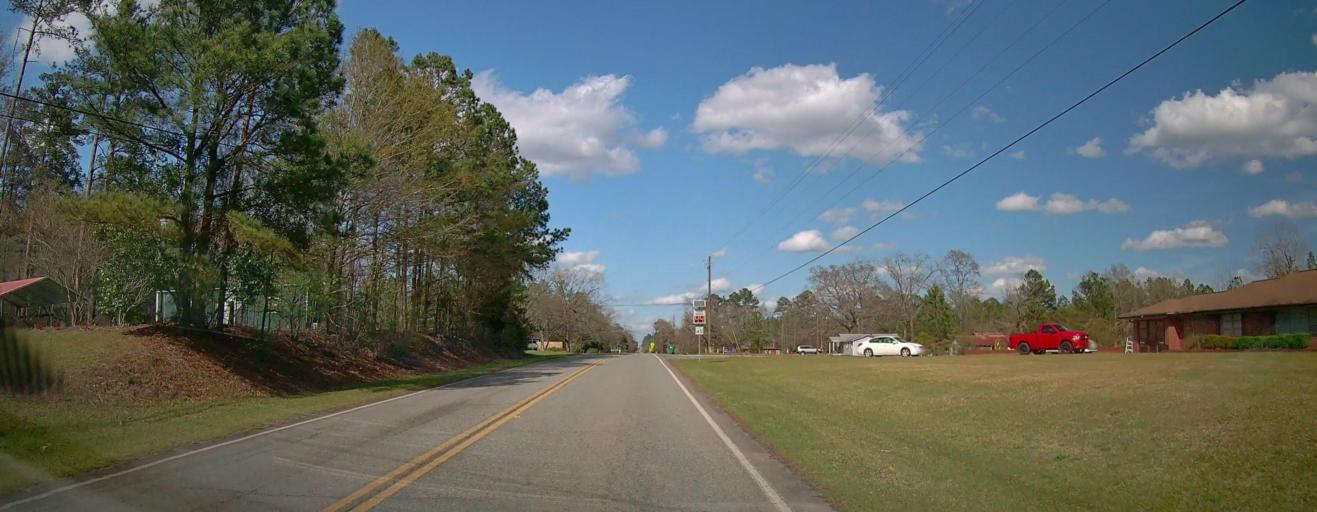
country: US
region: Georgia
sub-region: Wilkinson County
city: Gordon
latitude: 32.9722
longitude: -83.2835
